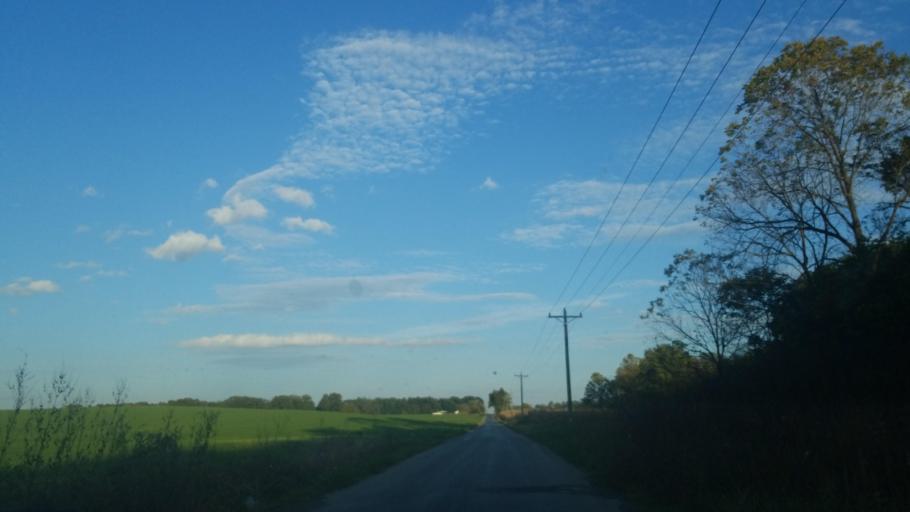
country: US
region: Illinois
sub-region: Saline County
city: Harrisburg
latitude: 37.8049
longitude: -88.6338
